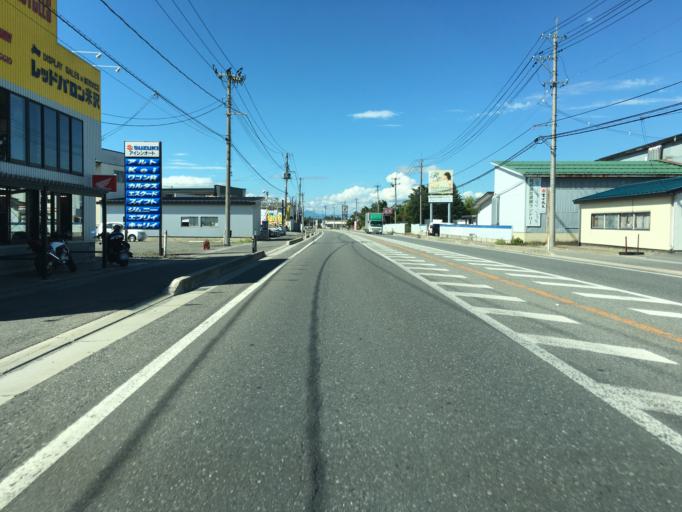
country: JP
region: Yamagata
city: Yonezawa
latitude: 37.9033
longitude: 140.1385
